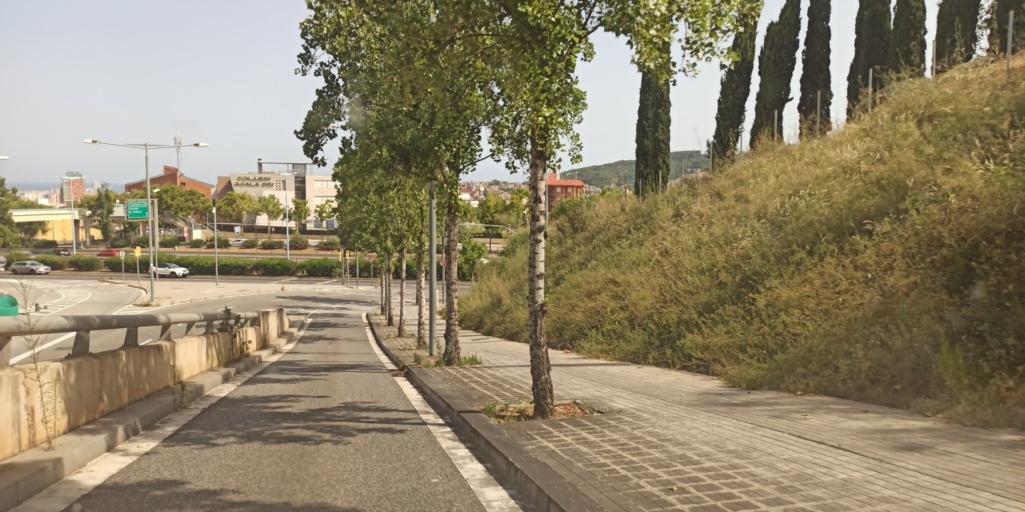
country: ES
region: Catalonia
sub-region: Provincia de Barcelona
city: Nou Barris
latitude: 41.4399
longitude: 2.1561
